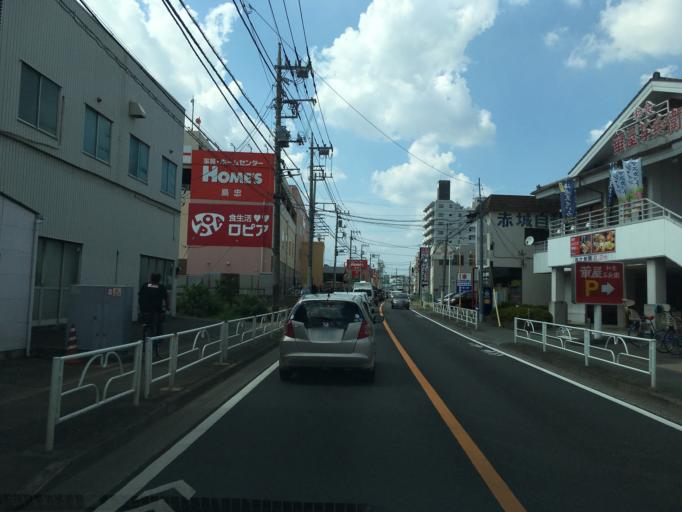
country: JP
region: Tokyo
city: Higashimurayama-shi
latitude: 35.7677
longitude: 139.4883
